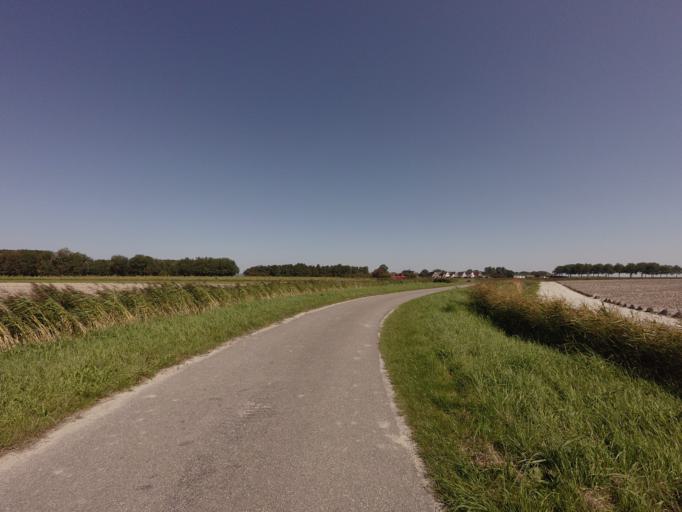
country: NL
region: Friesland
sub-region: Gemeente Dongeradeel
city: Anjum
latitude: 53.3992
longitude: 6.0785
